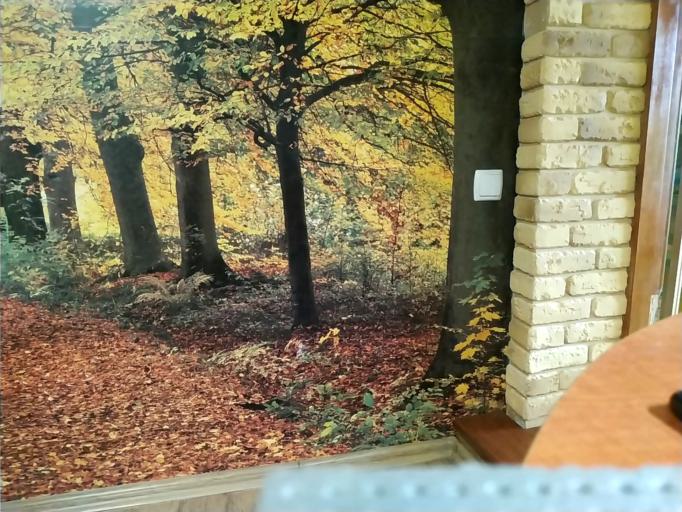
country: RU
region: Vladimir
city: Bavleny
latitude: 56.3702
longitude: 39.6062
